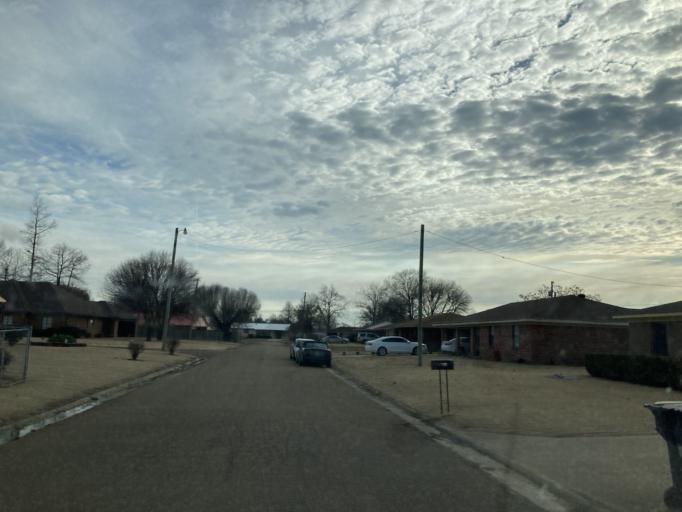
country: US
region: Mississippi
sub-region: Humphreys County
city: Belzoni
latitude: 33.1716
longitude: -90.5038
